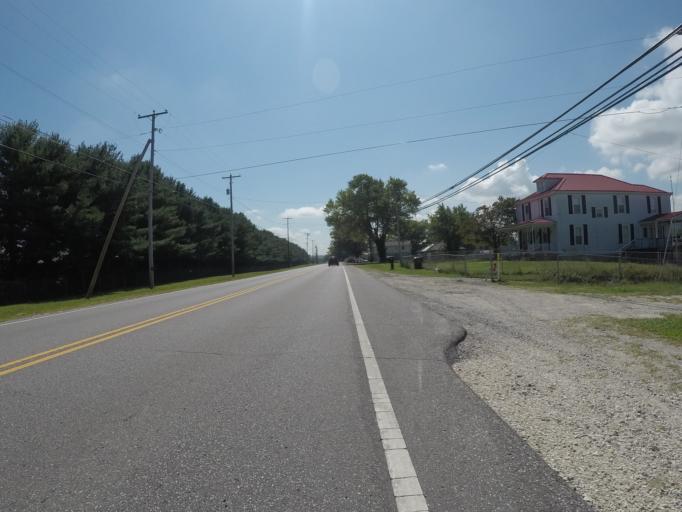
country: US
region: Ohio
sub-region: Lawrence County
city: South Point
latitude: 38.4269
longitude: -82.5922
